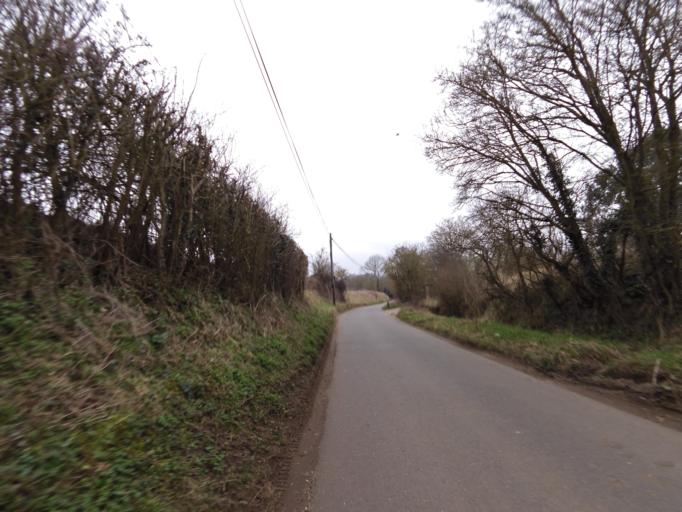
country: GB
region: England
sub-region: Suffolk
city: Framlingham
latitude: 52.2217
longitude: 1.3299
